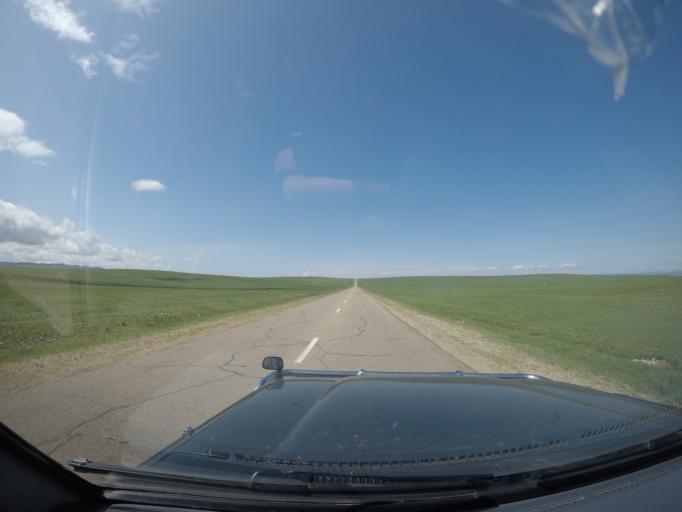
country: MN
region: Hentiy
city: Bayan
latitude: 47.2829
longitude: 110.9558
